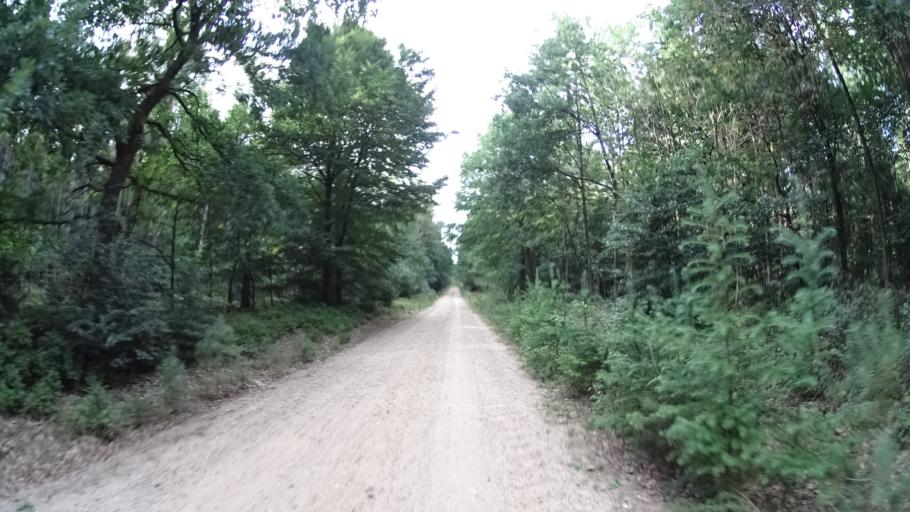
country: DE
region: Lower Saxony
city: Handeloh
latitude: 53.1808
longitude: 9.8844
